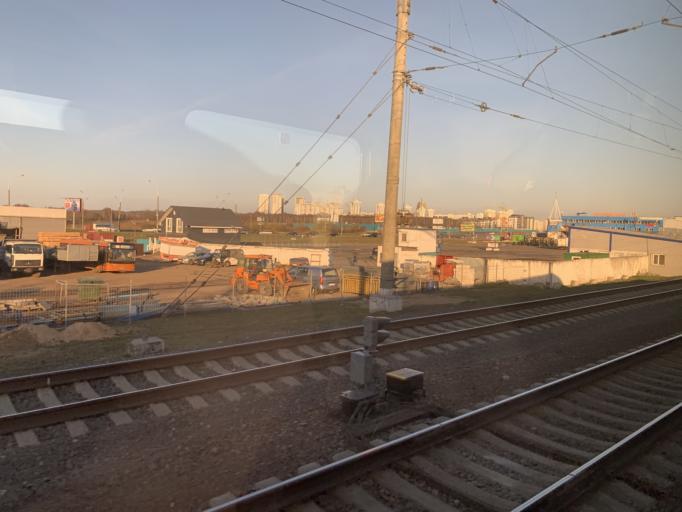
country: BY
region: Minsk
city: Zhdanovichy
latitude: 53.9418
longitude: 27.4362
